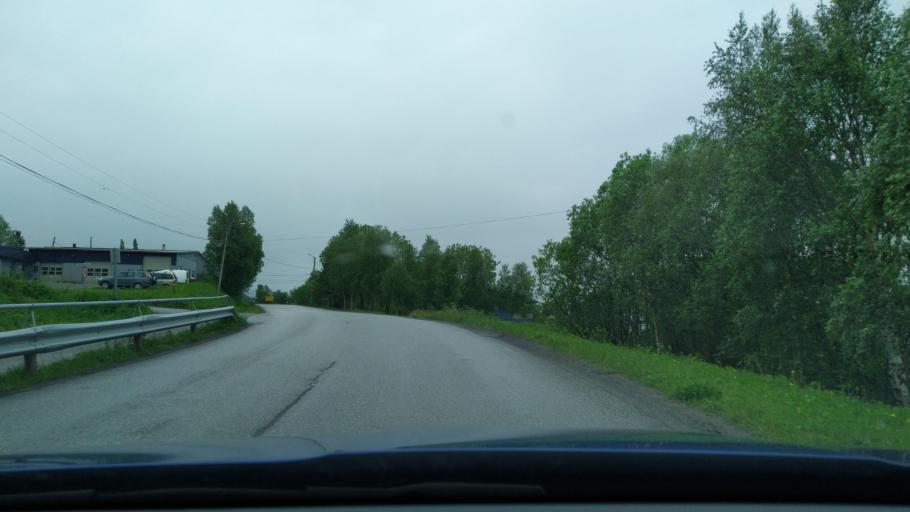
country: NO
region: Troms
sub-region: Dyroy
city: Brostadbotn
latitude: 69.0854
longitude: 17.6934
